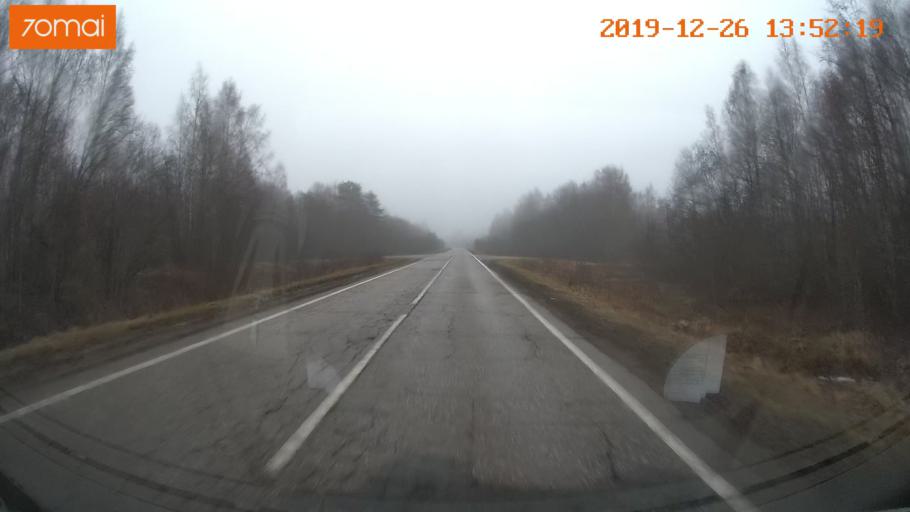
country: RU
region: Jaroslavl
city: Poshekhon'ye
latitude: 58.6333
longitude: 38.6006
